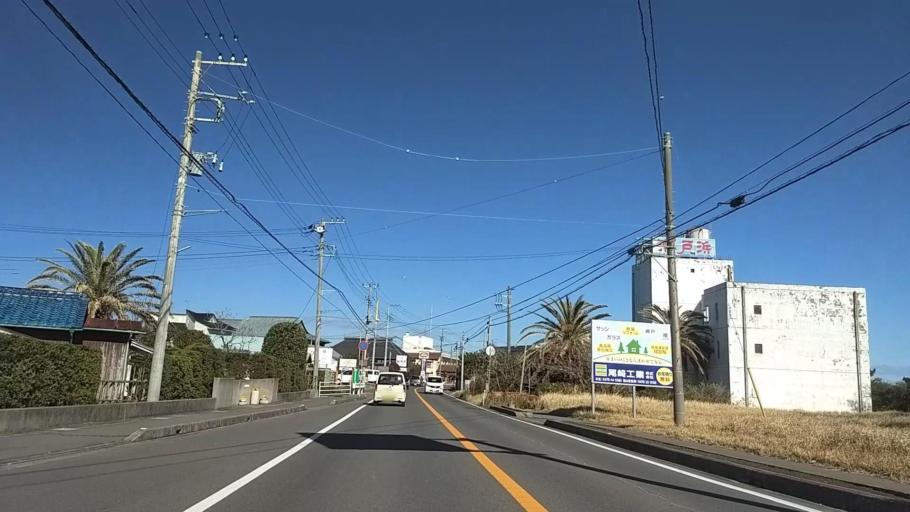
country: JP
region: Chiba
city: Tateyama
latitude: 34.9741
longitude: 139.9626
